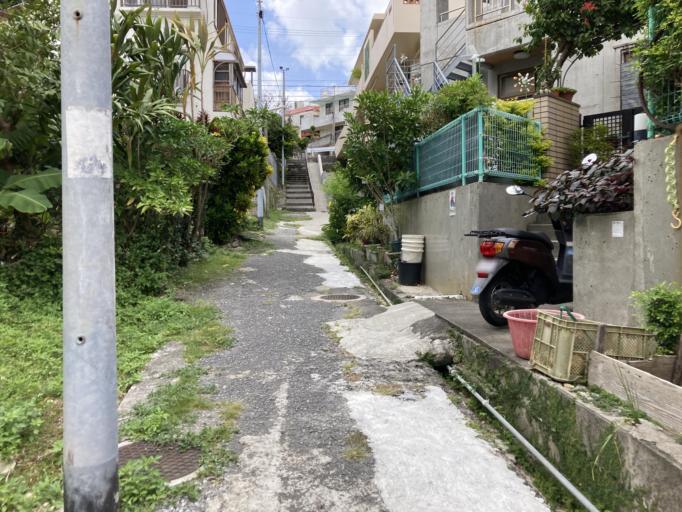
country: JP
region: Okinawa
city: Naha-shi
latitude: 26.2002
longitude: 127.6728
